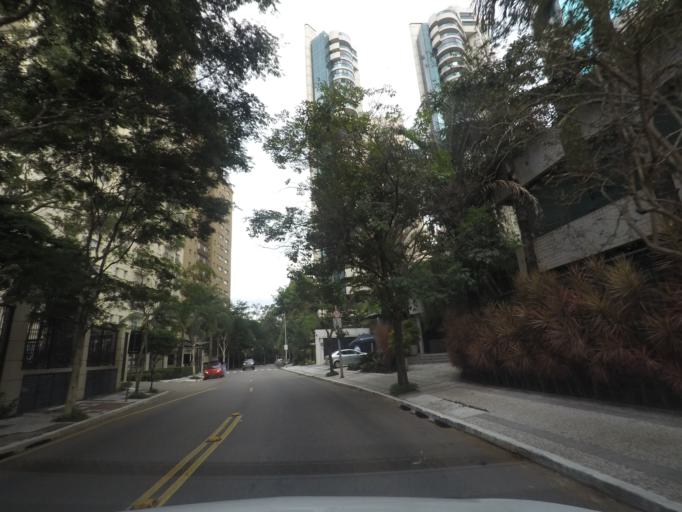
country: BR
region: Sao Paulo
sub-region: Taboao Da Serra
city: Taboao da Serra
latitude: -23.6325
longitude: -46.7247
